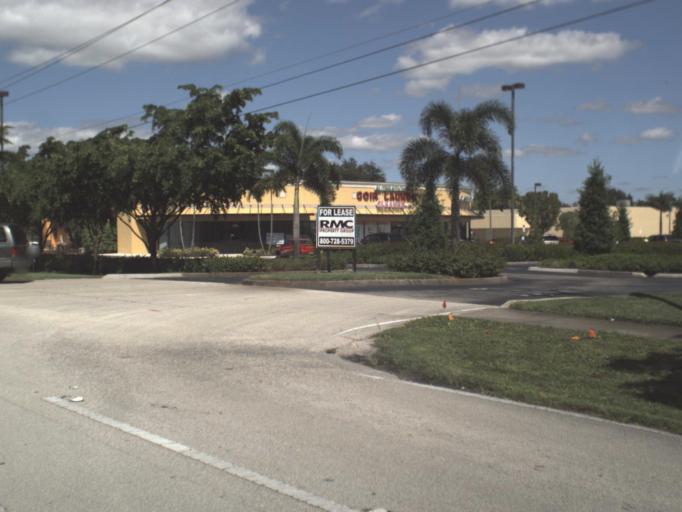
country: US
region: Florida
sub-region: Collier County
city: Lely
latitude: 26.1190
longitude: -81.7585
